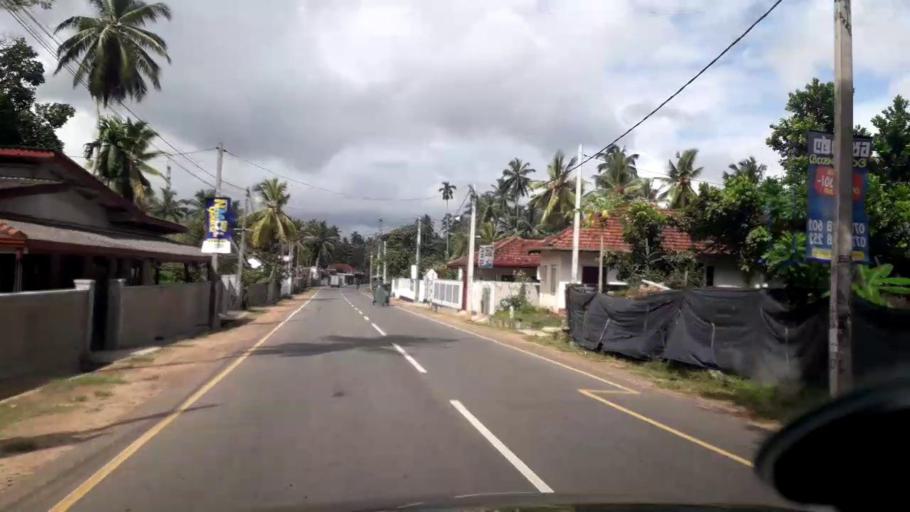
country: LK
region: Western
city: Panadura
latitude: 6.6695
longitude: 79.9384
